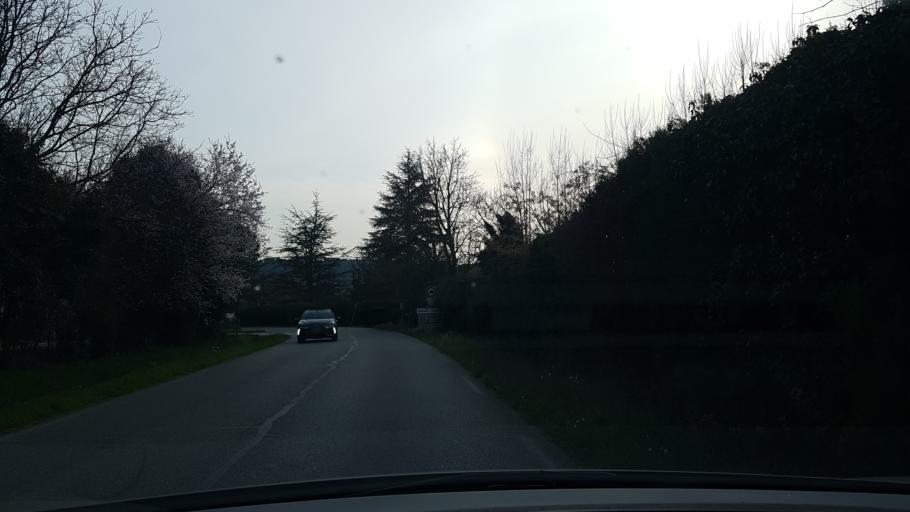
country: FR
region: Provence-Alpes-Cote d'Azur
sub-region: Departement des Bouches-du-Rhone
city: Simiane-Collongue
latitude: 43.4358
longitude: 5.4374
